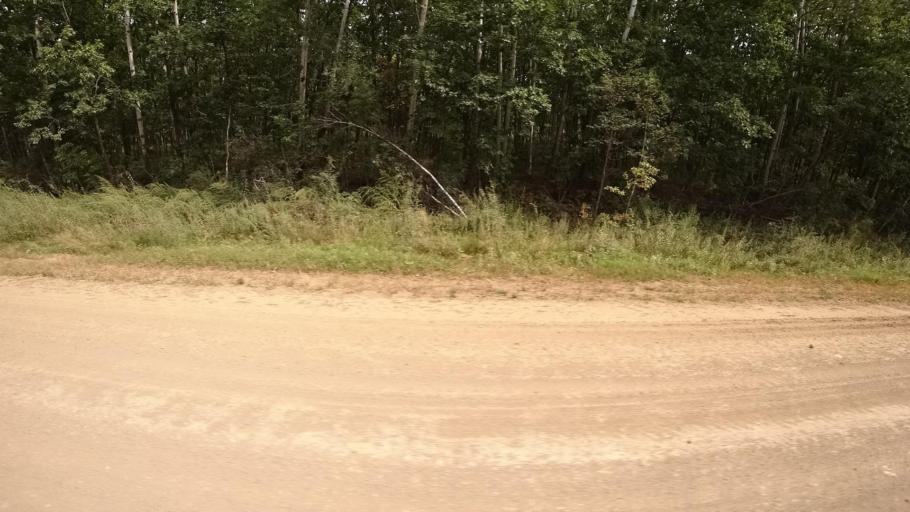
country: RU
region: Primorskiy
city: Yakovlevka
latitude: 44.4985
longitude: 133.5902
